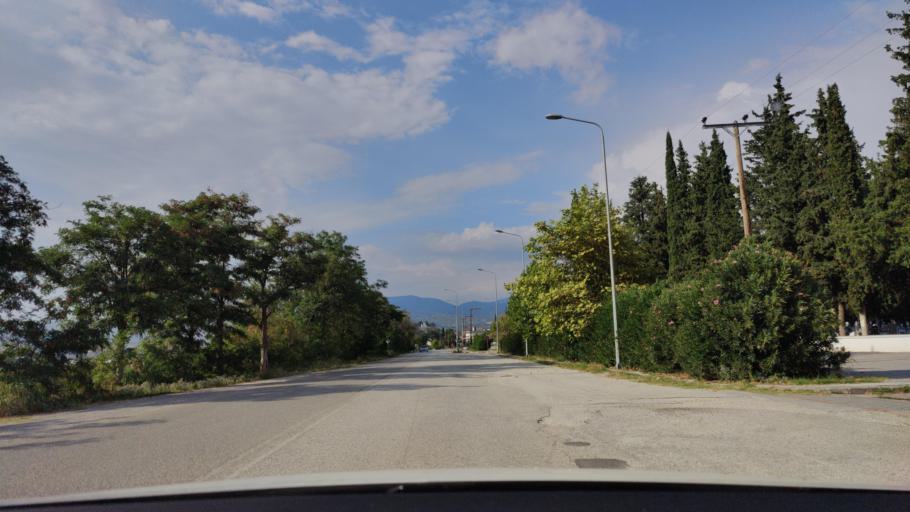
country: GR
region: Central Macedonia
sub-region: Nomos Serron
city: Sidirokastro
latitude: 41.2268
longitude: 23.3908
